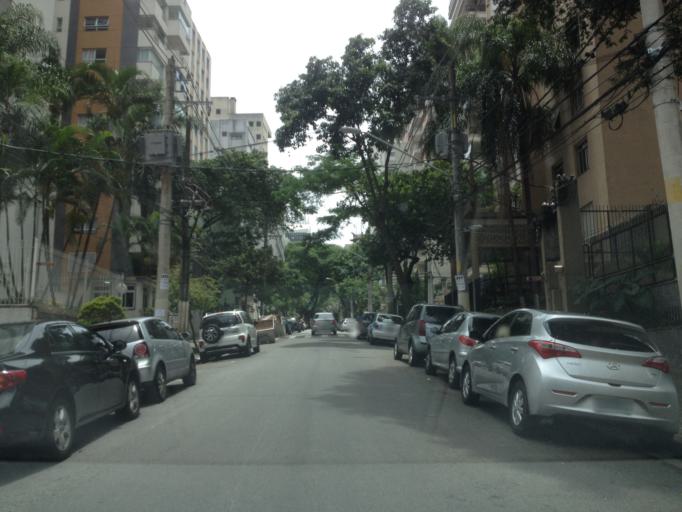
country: BR
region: Sao Paulo
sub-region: Sao Paulo
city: Sao Paulo
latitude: -23.5719
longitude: -46.6516
